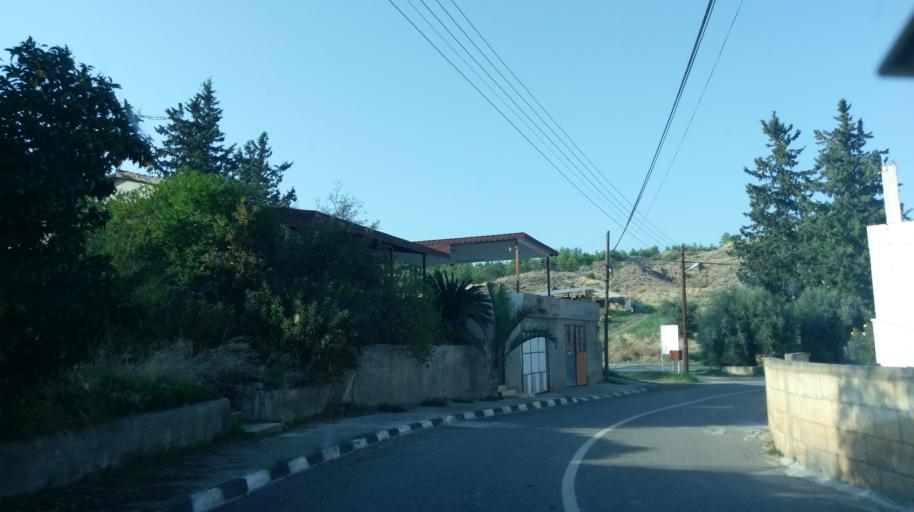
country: CY
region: Lefkosia
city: Lefka
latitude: 35.0907
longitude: 32.8431
